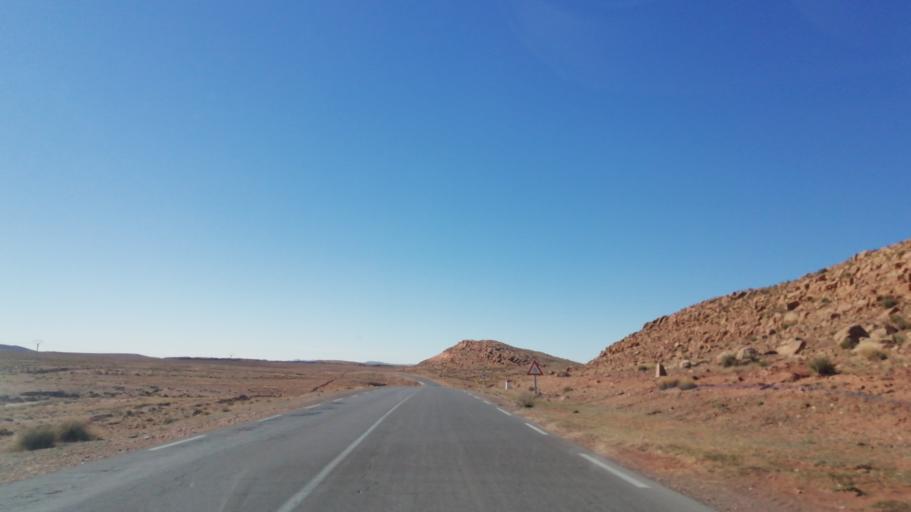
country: DZ
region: El Bayadh
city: El Bayadh
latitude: 33.6554
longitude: 1.4140
